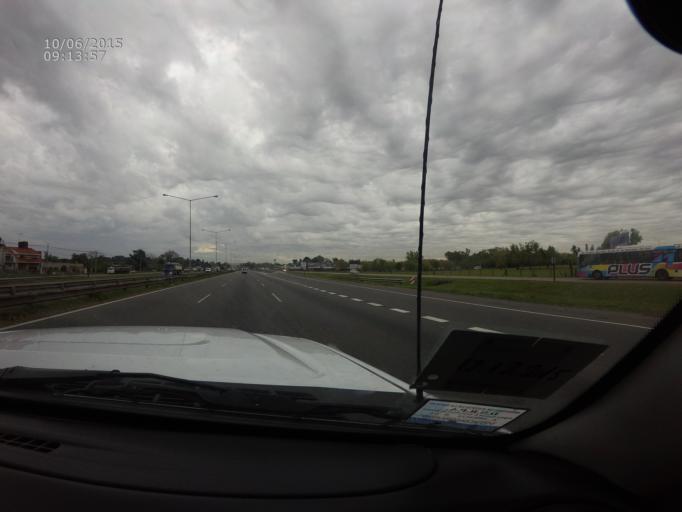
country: AR
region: Buenos Aires
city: Belen de Escobar
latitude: -34.3334
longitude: -58.8281
